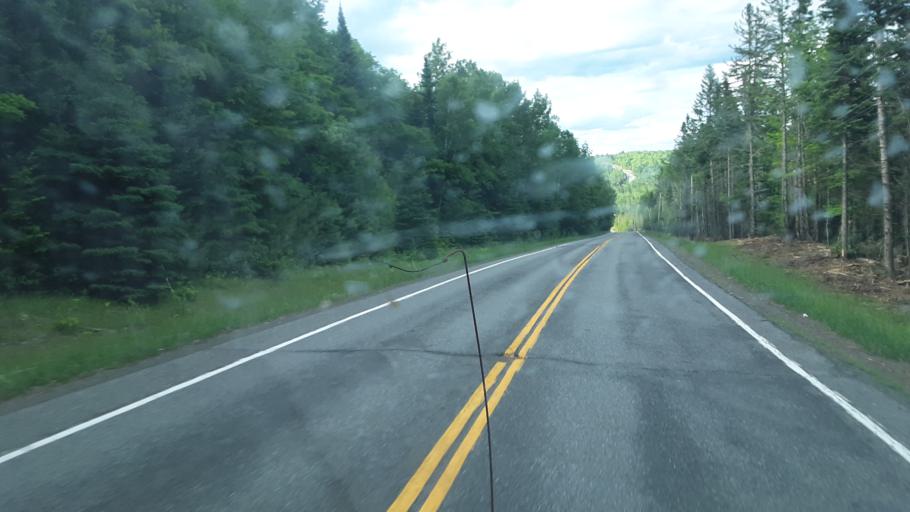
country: US
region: Maine
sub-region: Penobscot County
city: Patten
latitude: 46.1644
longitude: -68.3450
